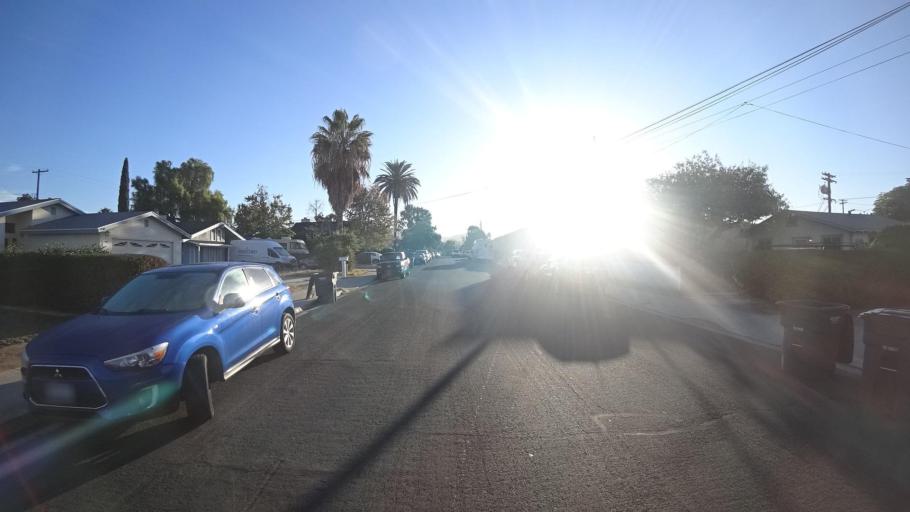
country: US
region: California
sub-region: San Diego County
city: Bostonia
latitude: 32.8088
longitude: -116.9376
